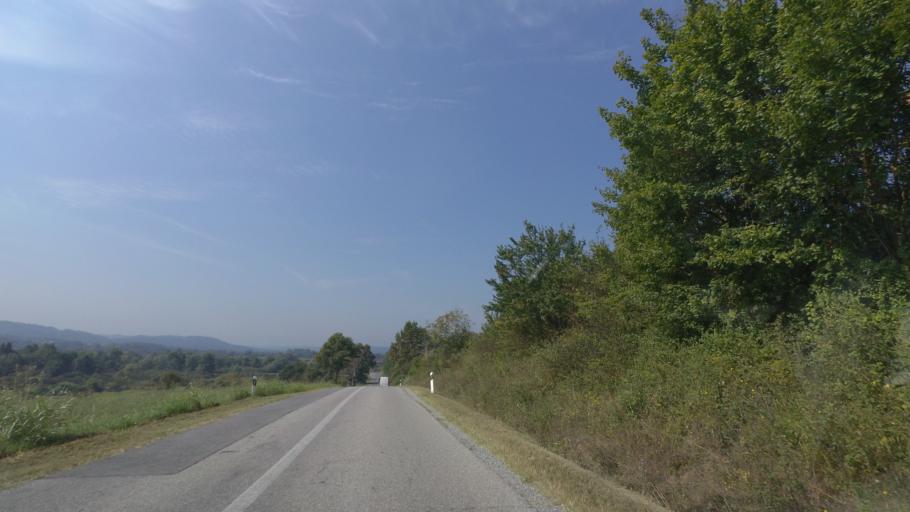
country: BA
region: Republika Srpska
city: Dobrljin
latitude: 45.1488
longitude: 16.4565
